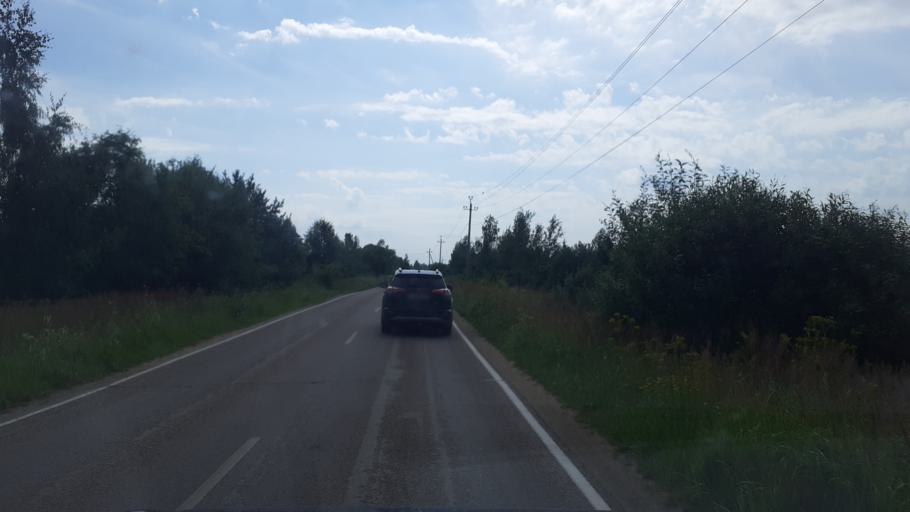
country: RU
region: Moskovskaya
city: Chupryakovo
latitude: 55.5640
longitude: 36.5681
